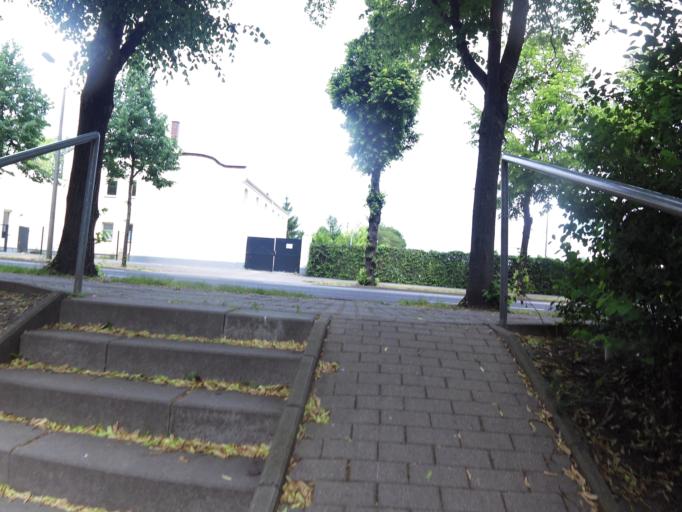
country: DE
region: Saxony
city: Leipzig
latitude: 51.3758
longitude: 12.3748
